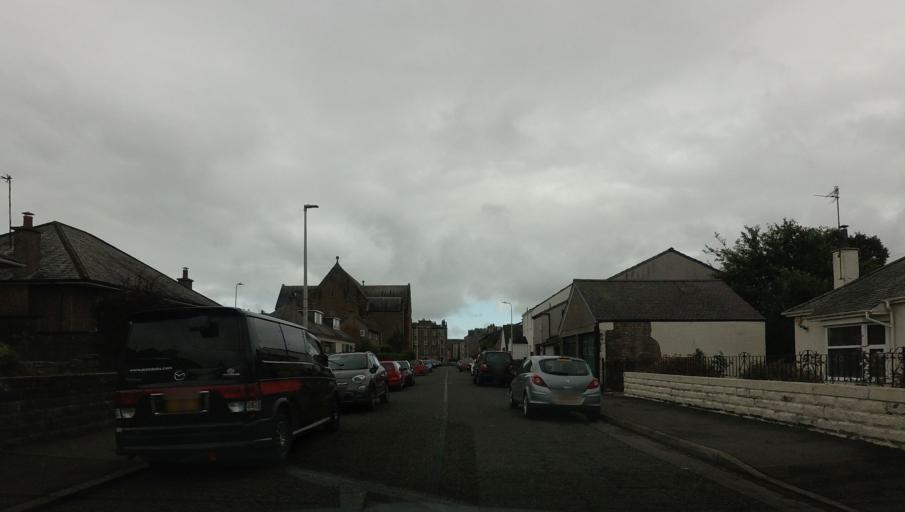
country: GB
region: Scotland
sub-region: Dundee City
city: Dundee
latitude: 56.4572
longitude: -2.9991
